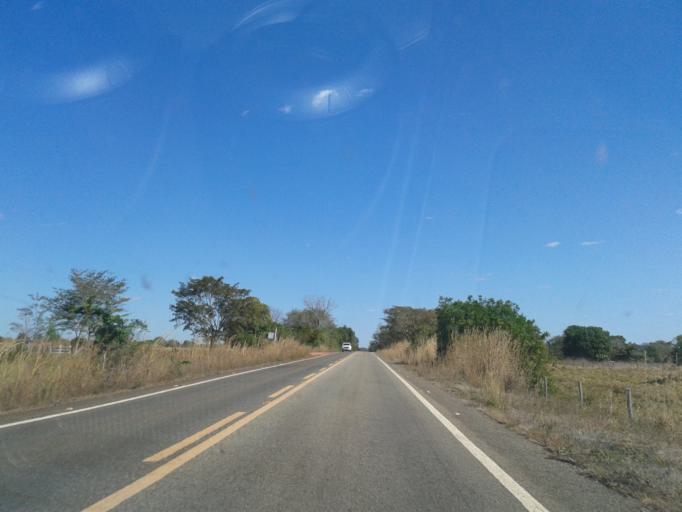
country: BR
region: Goias
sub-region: Sao Miguel Do Araguaia
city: Sao Miguel do Araguaia
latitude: -13.6612
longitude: -50.3240
